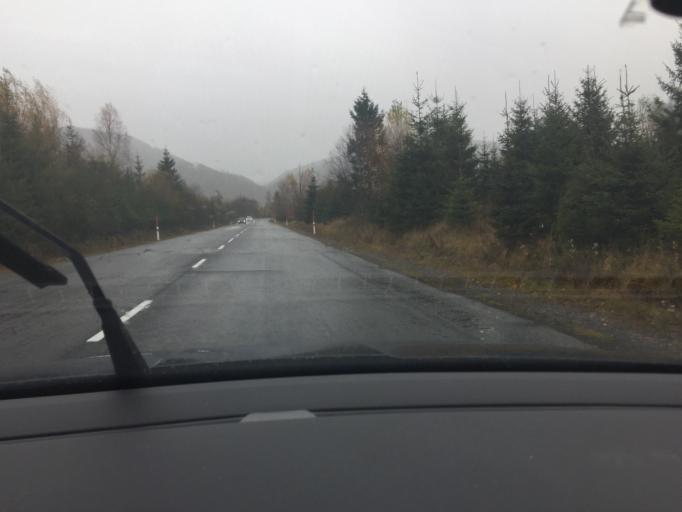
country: SK
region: Presovsky
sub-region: Okres Poprad
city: Nova Lesna
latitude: 49.1799
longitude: 20.2921
